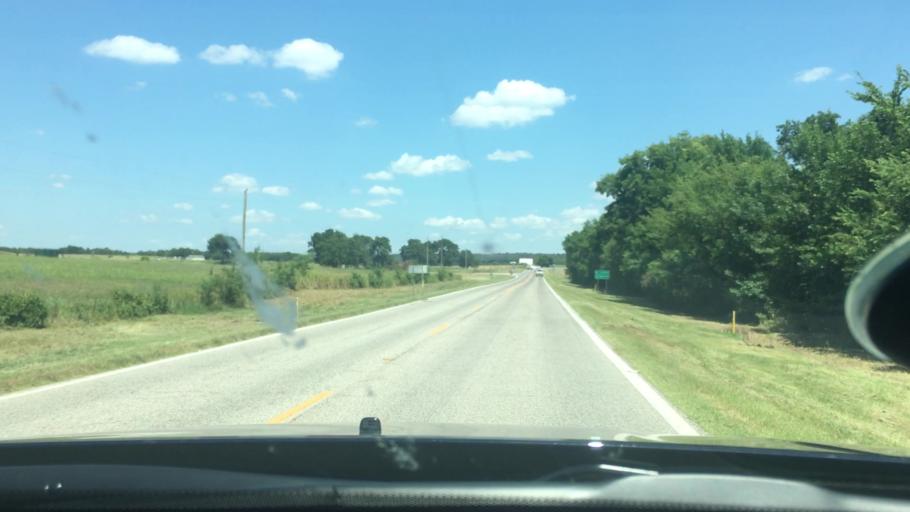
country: US
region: Oklahoma
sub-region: Carter County
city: Dickson
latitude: 34.2861
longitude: -96.9682
